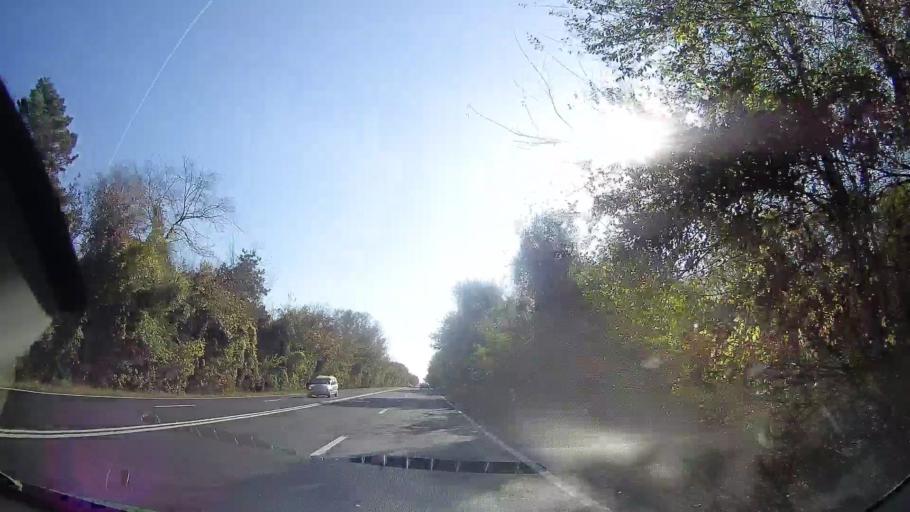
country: RO
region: Constanta
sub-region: Comuna Douazeci si Trei August
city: Dulcesti
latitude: 43.8669
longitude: 28.5749
